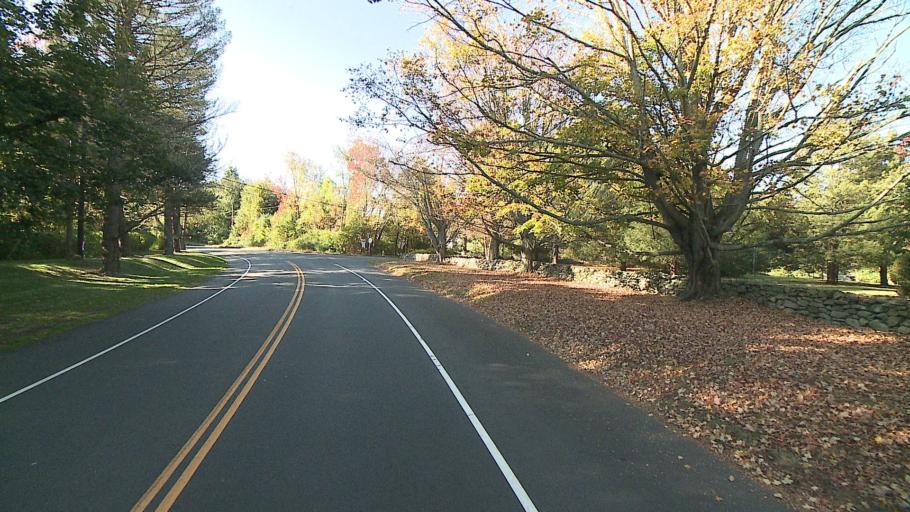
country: US
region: Connecticut
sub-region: Fairfield County
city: Wilton
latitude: 41.1736
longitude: -73.3945
